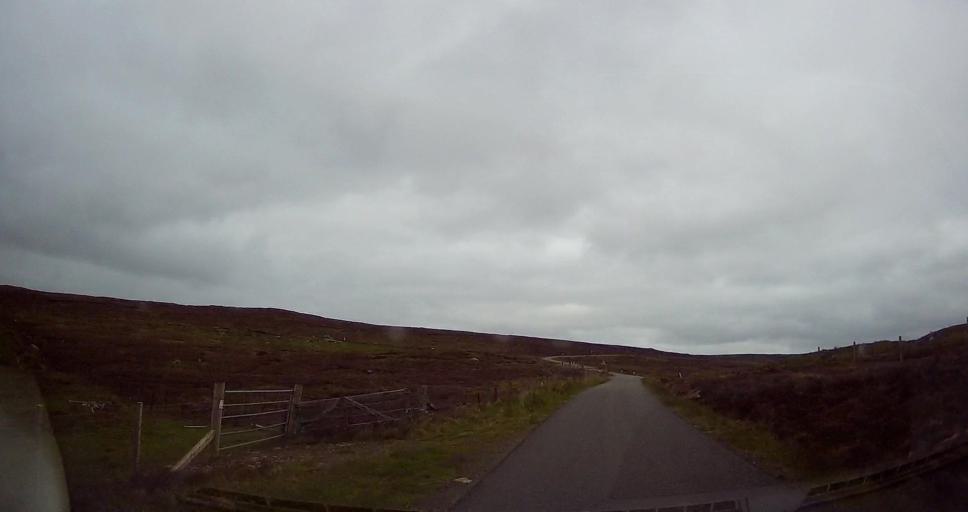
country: GB
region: Scotland
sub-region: Shetland Islands
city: Lerwick
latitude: 60.3107
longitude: -1.3386
